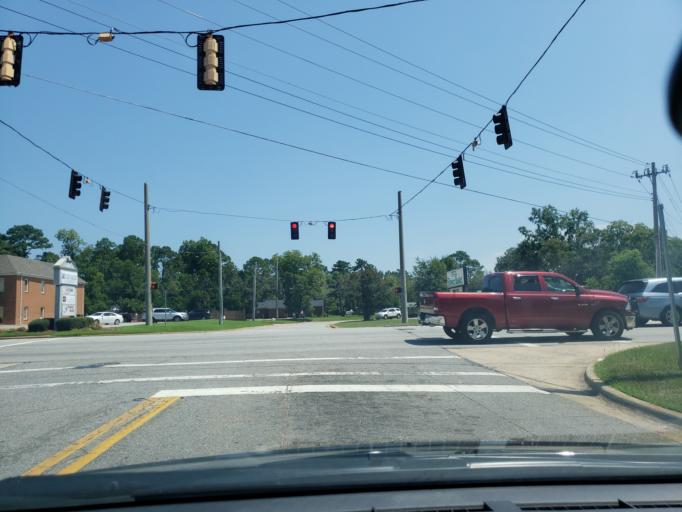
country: US
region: Georgia
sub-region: Dougherty County
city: Albany
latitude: 31.6032
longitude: -84.2045
